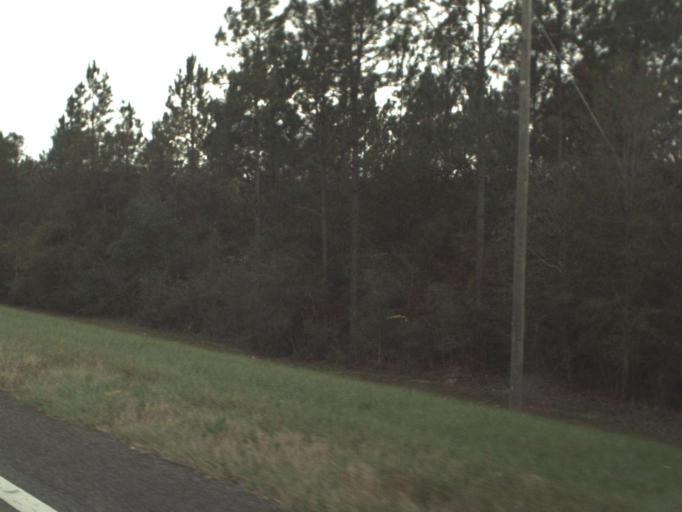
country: US
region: Florida
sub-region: Escambia County
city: Molino
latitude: 30.7646
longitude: -87.3413
